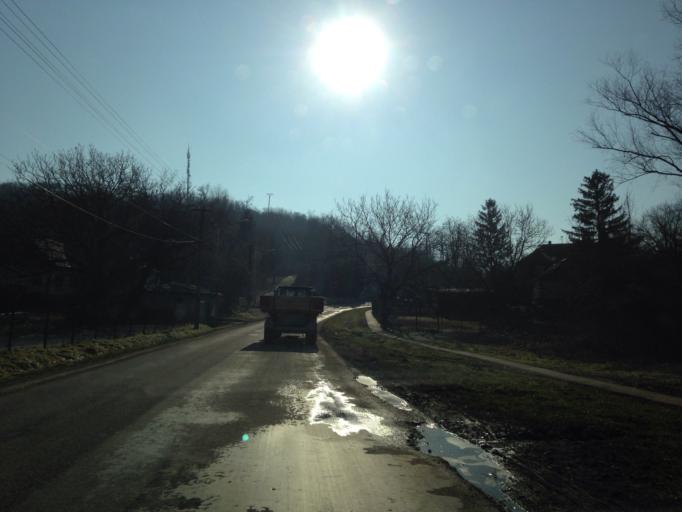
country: SK
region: Nitriansky
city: Svodin
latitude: 47.9538
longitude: 18.4126
